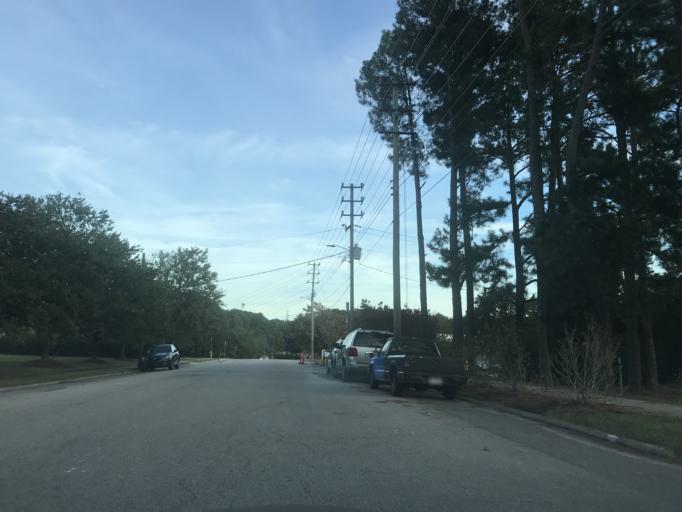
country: US
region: North Carolina
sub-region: Wake County
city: Raleigh
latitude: 35.8248
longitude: -78.6116
